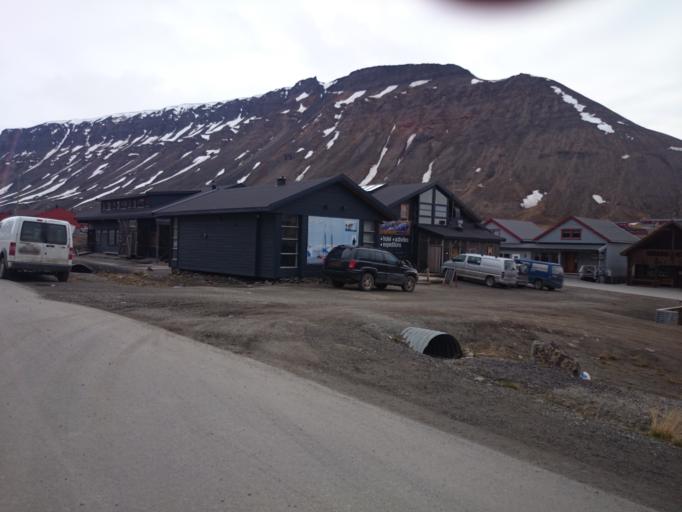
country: SJ
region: Svalbard
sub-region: Spitsbergen
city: Longyearbyen
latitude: 78.2172
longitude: 15.6382
